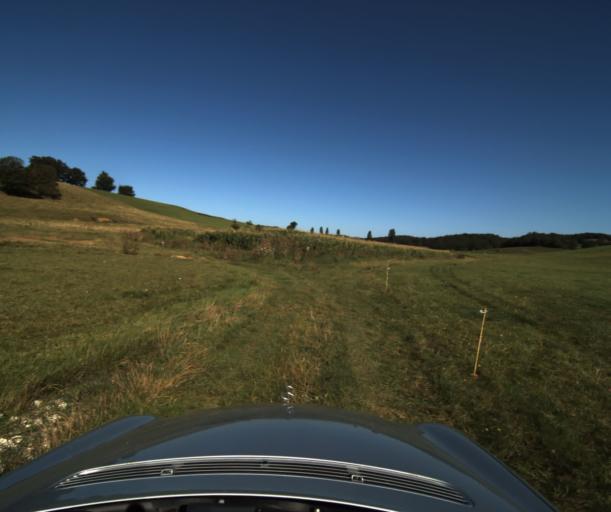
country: FR
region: Midi-Pyrenees
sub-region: Departement de l'Ariege
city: Lavelanet
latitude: 42.9818
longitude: 1.9067
